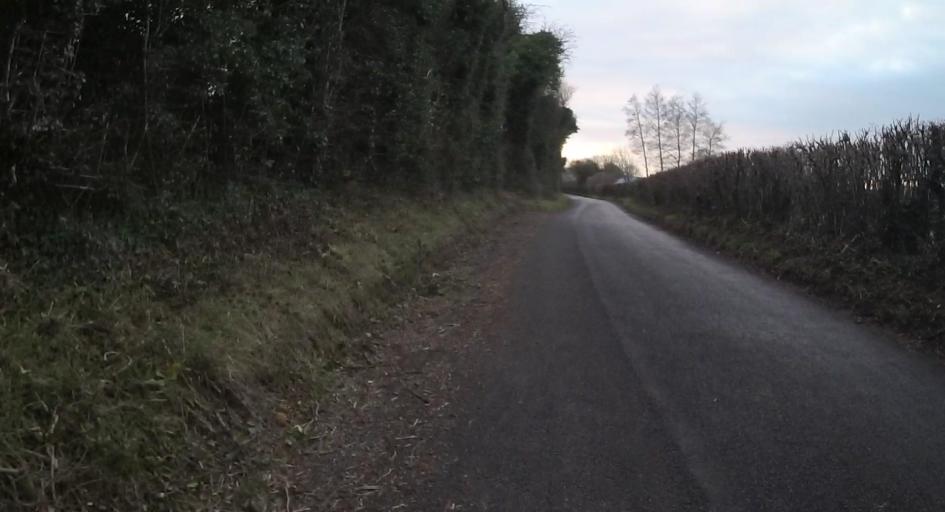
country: GB
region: England
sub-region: Hampshire
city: Swanmore
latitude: 51.0243
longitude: -1.1574
